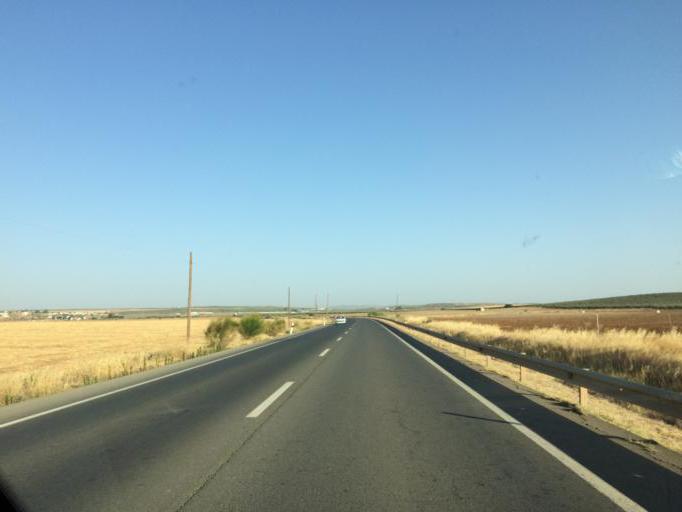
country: ES
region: Andalusia
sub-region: Provincia de Malaga
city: Humilladero
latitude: 37.0606
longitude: -4.6940
